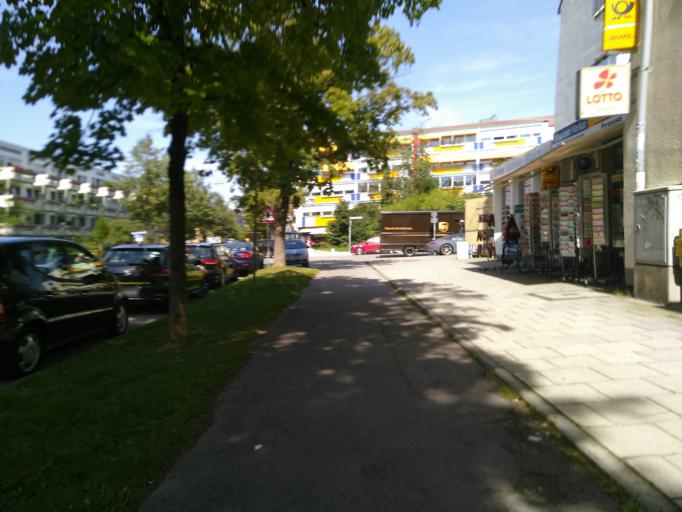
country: DE
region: Bavaria
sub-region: Upper Bavaria
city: Munich
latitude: 48.1054
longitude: 11.5743
